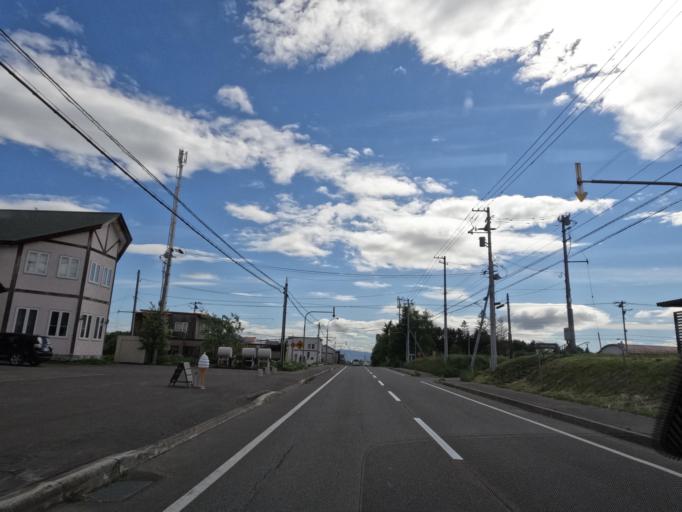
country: JP
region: Hokkaido
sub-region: Asahikawa-shi
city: Asahikawa
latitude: 43.8295
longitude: 142.5278
